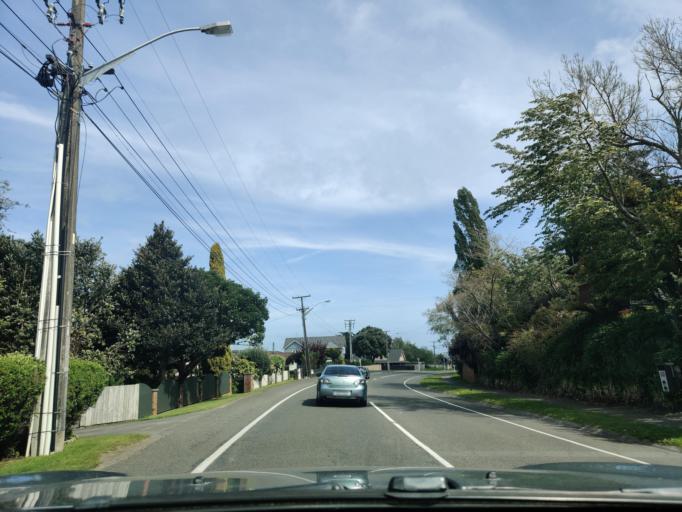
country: NZ
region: Manawatu-Wanganui
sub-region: Wanganui District
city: Wanganui
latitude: -39.9116
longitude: 175.0265
